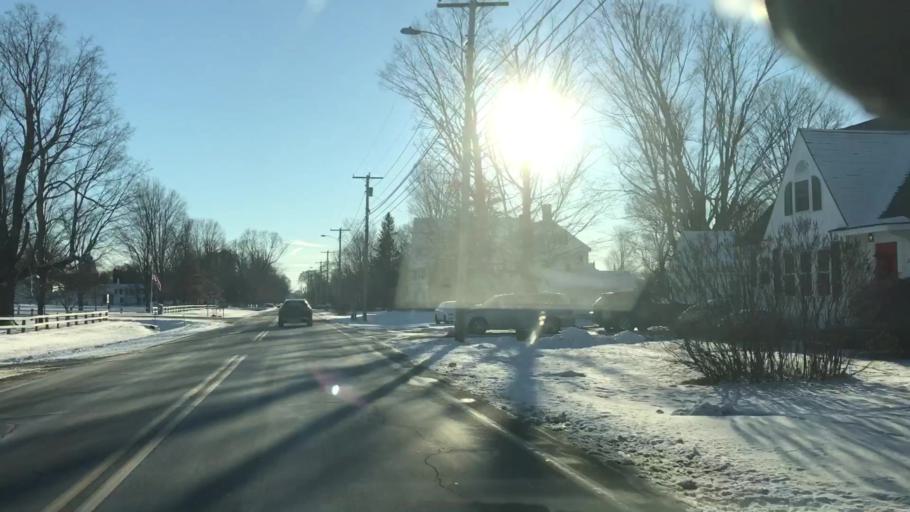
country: US
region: New Hampshire
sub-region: Grafton County
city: Haverhill
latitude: 44.0352
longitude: -72.0630
